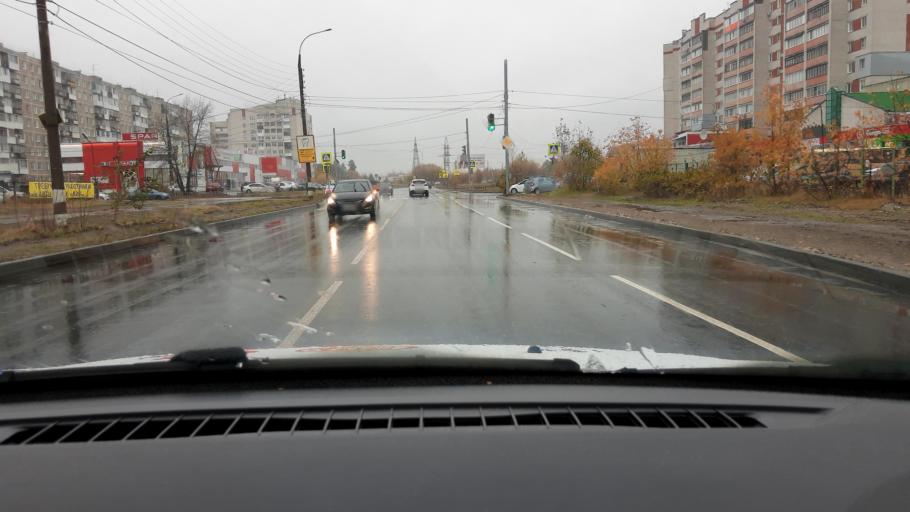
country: RU
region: Nizjnij Novgorod
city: Dzerzhinsk
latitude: 56.2326
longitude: 43.4096
